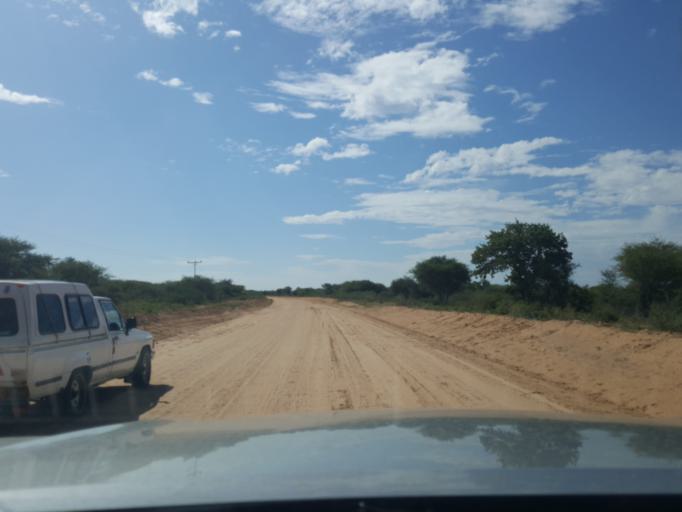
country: BW
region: Kweneng
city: Khudumelapye
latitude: -23.8143
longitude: 24.8222
